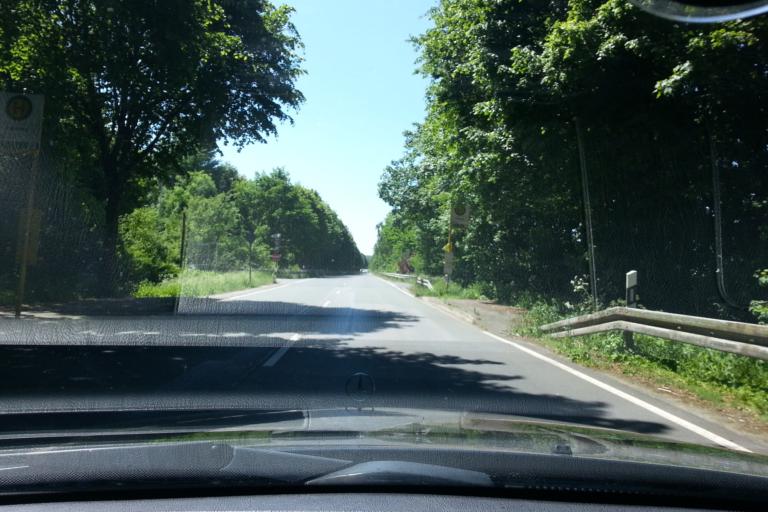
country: DE
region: North Rhine-Westphalia
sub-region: Regierungsbezirk Munster
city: Haltern
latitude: 51.7053
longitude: 7.1426
